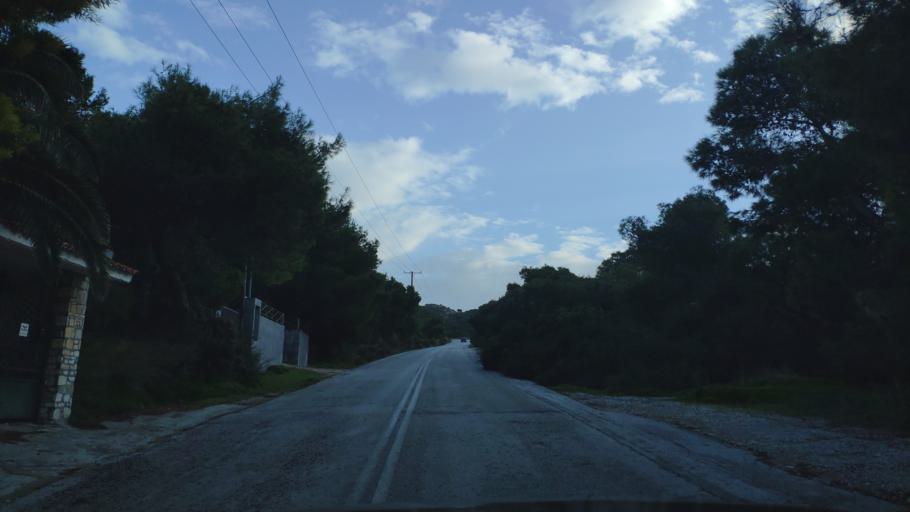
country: GR
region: Attica
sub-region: Nomarchia Anatolikis Attikis
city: Limin Mesoyaias
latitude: 37.9142
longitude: 24.0145
